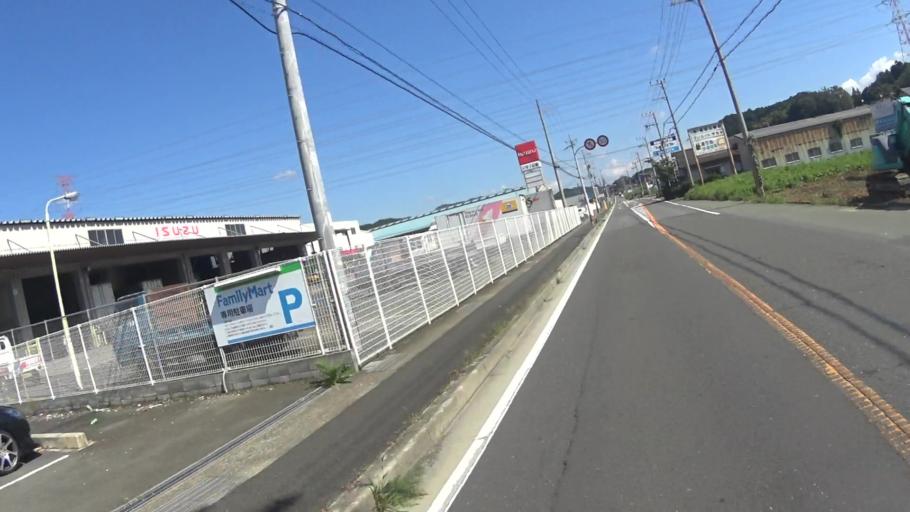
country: JP
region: Kyoto
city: Ayabe
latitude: 35.3186
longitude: 135.2862
